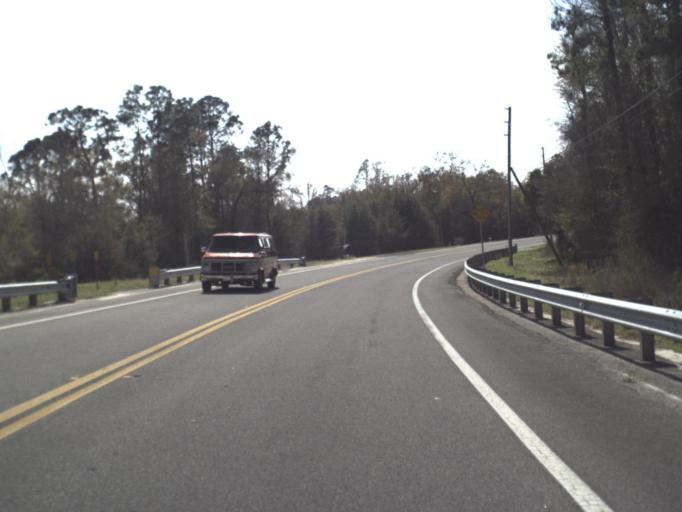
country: US
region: Florida
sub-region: Wakulla County
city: Crawfordville
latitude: 30.0689
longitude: -84.4517
